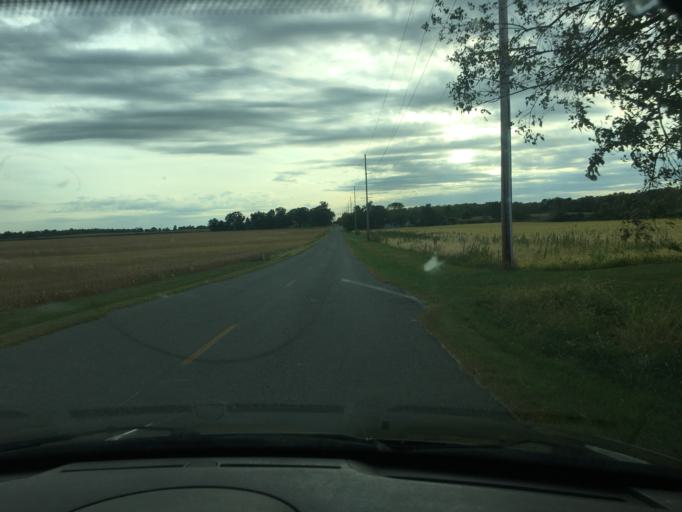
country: US
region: Ohio
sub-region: Logan County
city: West Liberty
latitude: 40.2808
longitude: -83.6995
